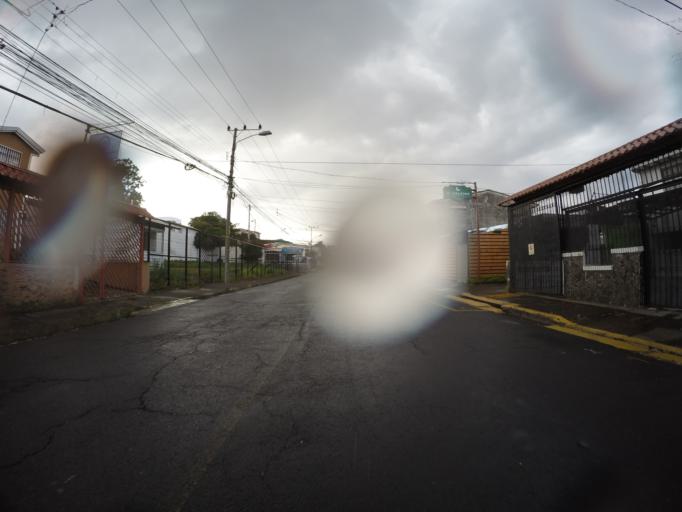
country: CR
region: San Jose
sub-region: Canton de Goicoechea
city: Guadalupe
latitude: 9.9372
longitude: -84.0615
